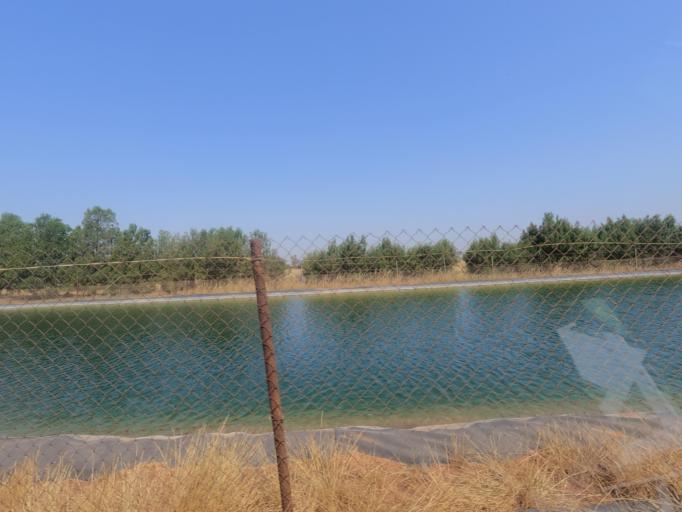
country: CY
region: Ammochostos
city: Avgorou
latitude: 35.0154
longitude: 33.8154
